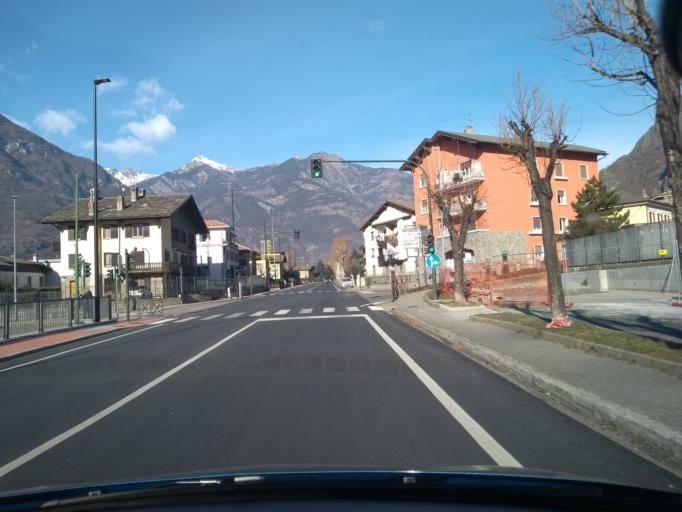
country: IT
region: Aosta Valley
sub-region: Valle d'Aosta
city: Verres
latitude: 45.6624
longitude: 7.6918
